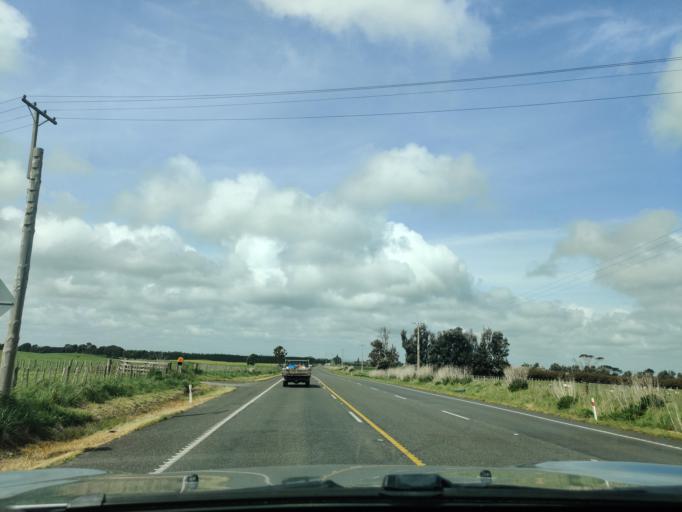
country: NZ
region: Taranaki
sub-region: South Taranaki District
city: Patea
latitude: -39.7665
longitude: 174.6104
